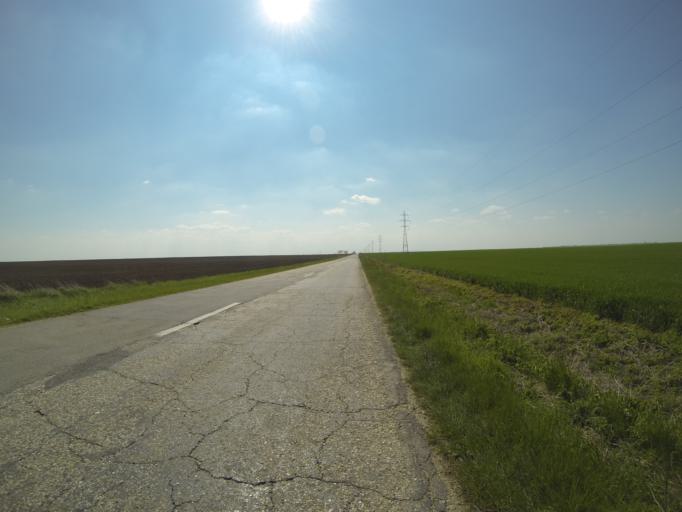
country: RO
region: Mehedinti
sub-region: Comuna Darvari
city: Gemeni
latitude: 44.1558
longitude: 23.1289
